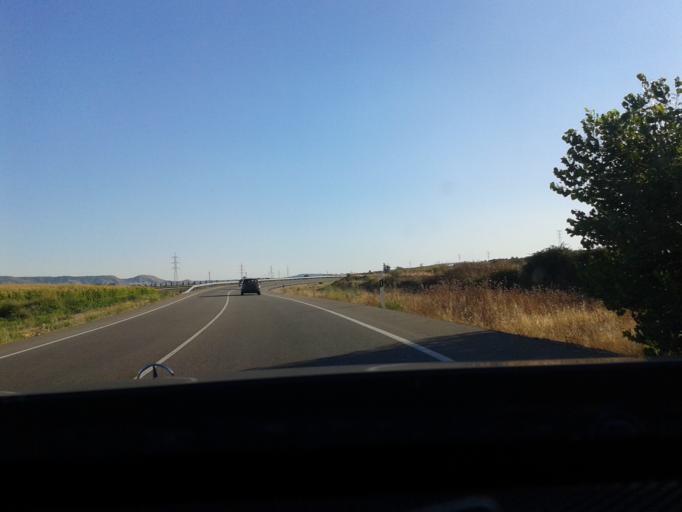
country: ES
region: Castille-La Mancha
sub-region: Provincia de Guadalajara
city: Quer
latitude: 40.5938
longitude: -3.2639
